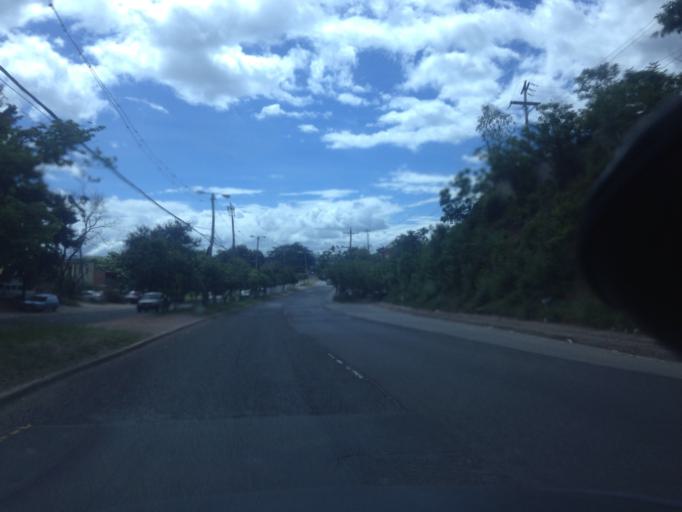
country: HN
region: Francisco Morazan
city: Tegucigalpa
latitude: 14.0721
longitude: -87.1779
